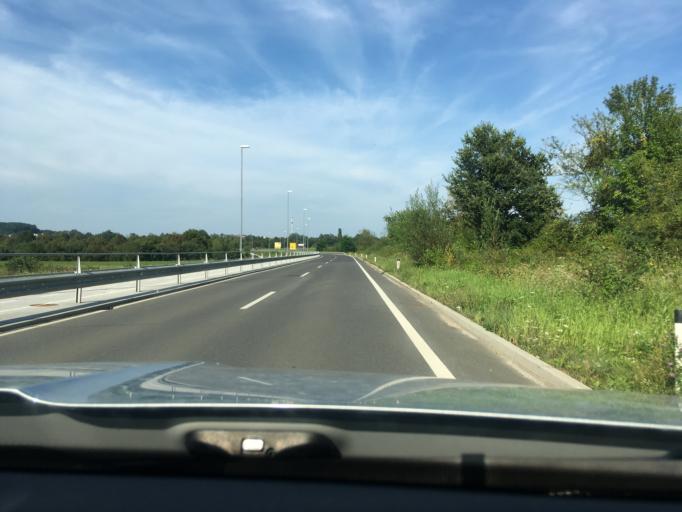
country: SI
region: Crnomelj
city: Crnomelj
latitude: 45.5663
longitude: 15.1764
